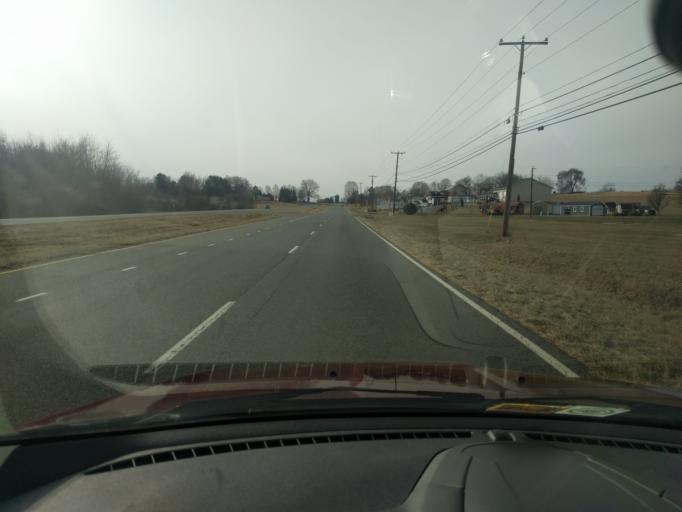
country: US
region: Virginia
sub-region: Augusta County
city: Lyndhurst
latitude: 38.0506
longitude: -78.9683
